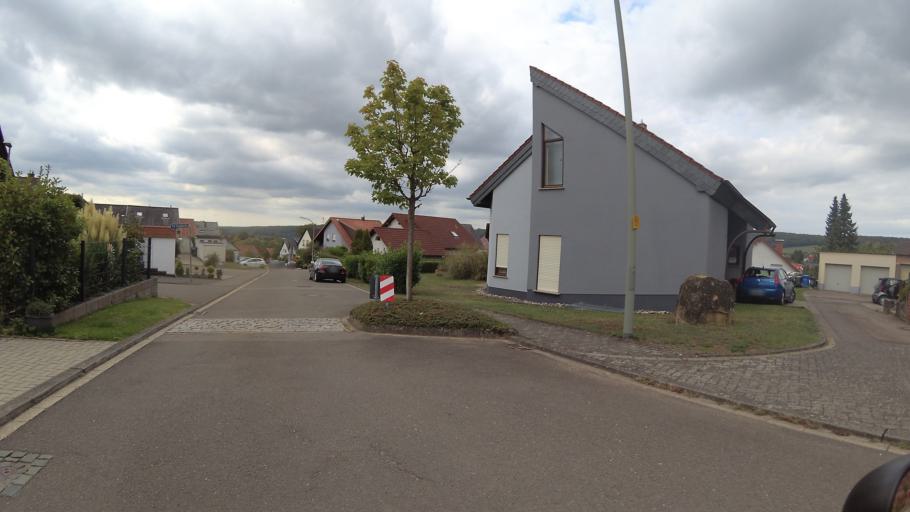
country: DE
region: Saarland
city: Kleinblittersdorf
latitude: 49.1669
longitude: 7.0948
